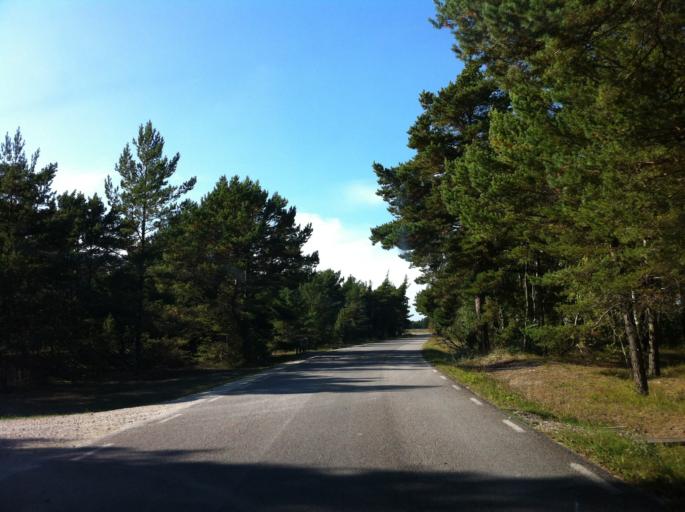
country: SE
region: Gotland
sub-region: Gotland
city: Slite
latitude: 57.9714
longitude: 19.2517
